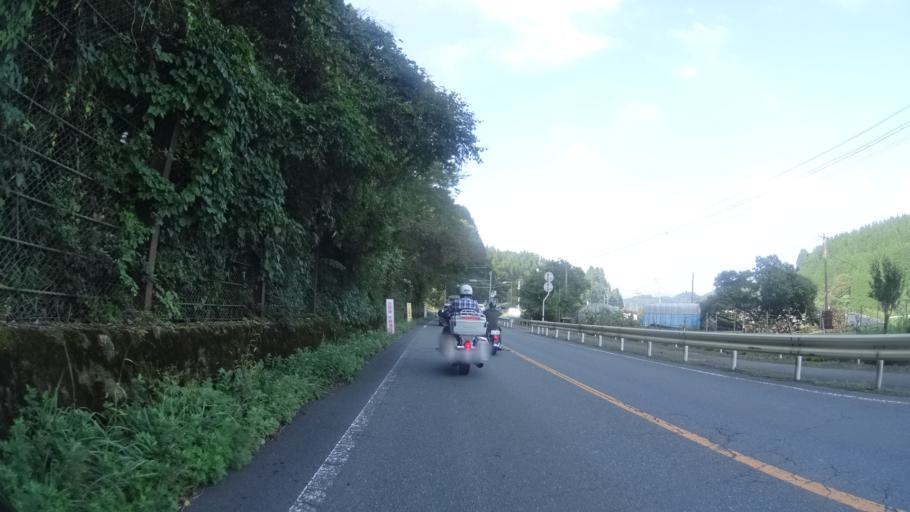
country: JP
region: Kumamoto
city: Aso
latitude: 33.0921
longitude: 131.0667
